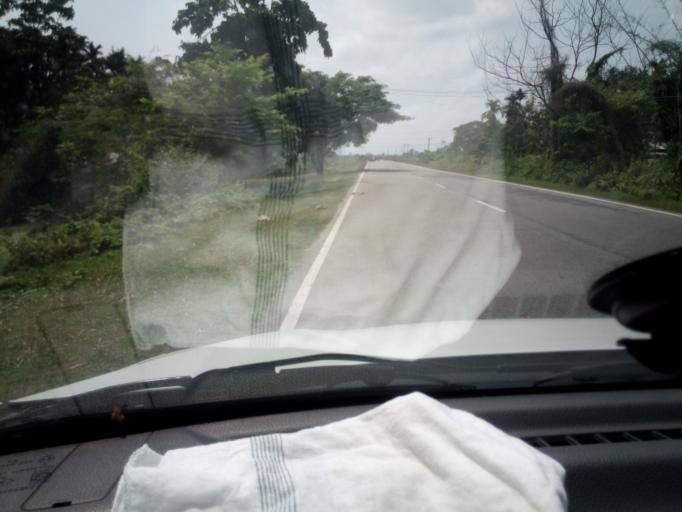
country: IN
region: Assam
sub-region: Udalguri
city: Udalguri
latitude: 26.7279
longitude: 92.1787
